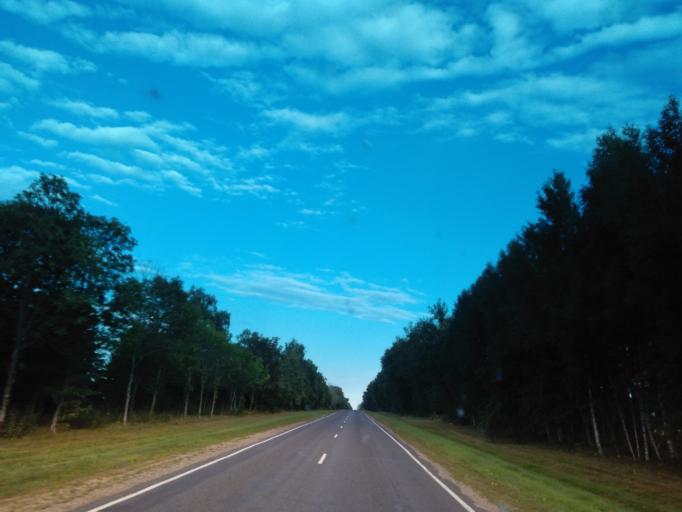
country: BY
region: Minsk
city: Uzda
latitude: 53.4362
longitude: 27.3335
